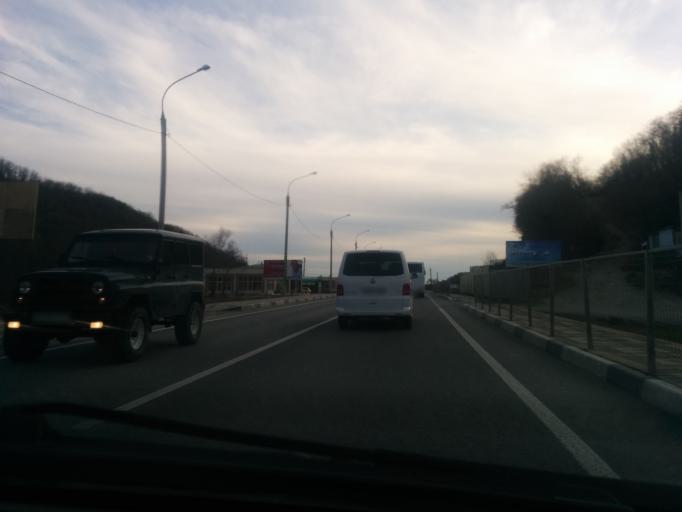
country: RU
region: Krasnodarskiy
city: Ol'ginka
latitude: 44.2084
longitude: 38.8916
